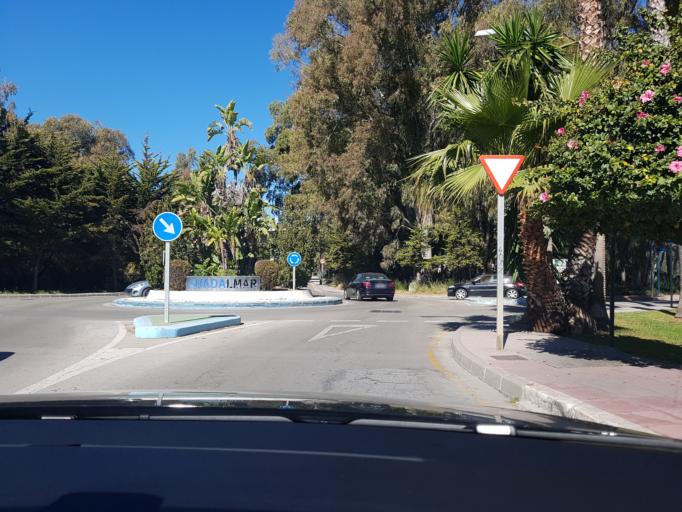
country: ES
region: Andalusia
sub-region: Provincia de Malaga
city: Torremolinos
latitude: 36.6688
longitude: -4.4648
